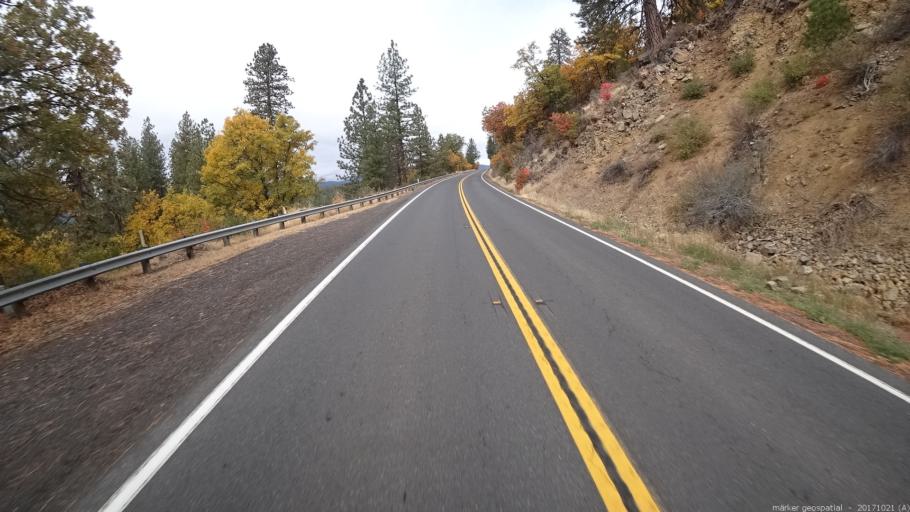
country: US
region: California
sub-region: Shasta County
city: Burney
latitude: 41.0297
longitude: -121.6271
